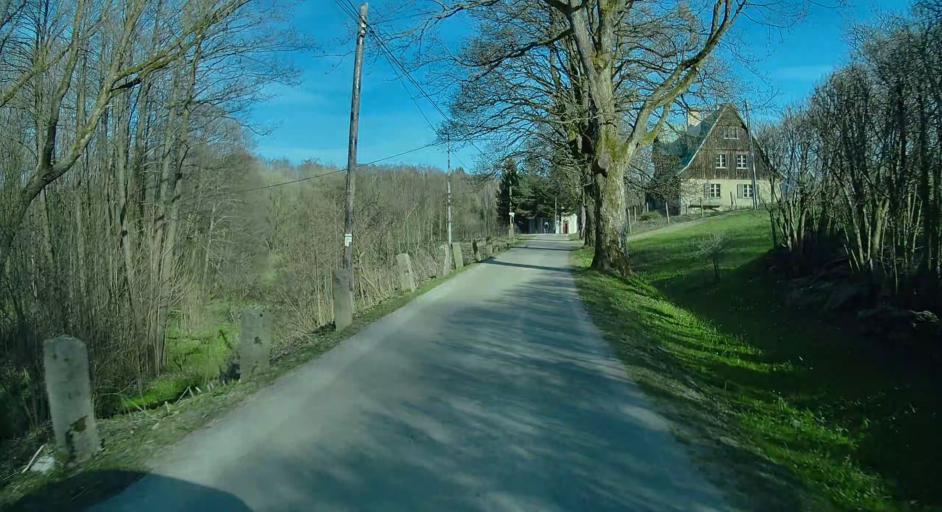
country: PL
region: Lower Silesian Voivodeship
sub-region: Powiat klodzki
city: Lewin Klodzki
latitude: 50.3798
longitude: 16.2773
